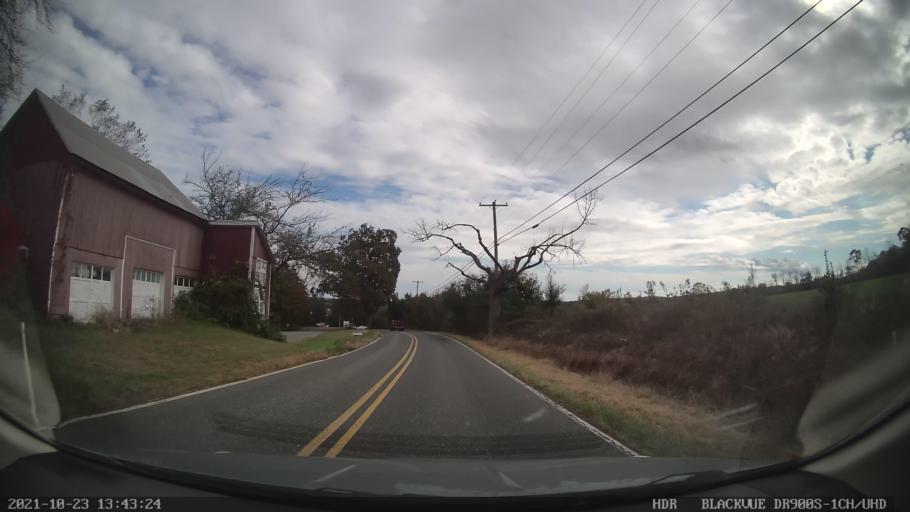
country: US
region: Pennsylvania
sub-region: Montgomery County
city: East Greenville
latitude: 40.4007
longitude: -75.5422
